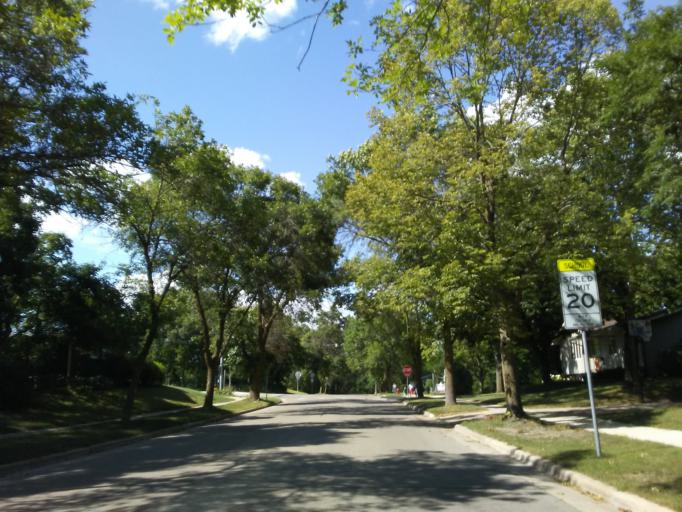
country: US
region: Wisconsin
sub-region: Dane County
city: Middleton
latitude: 43.0668
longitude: -89.4933
